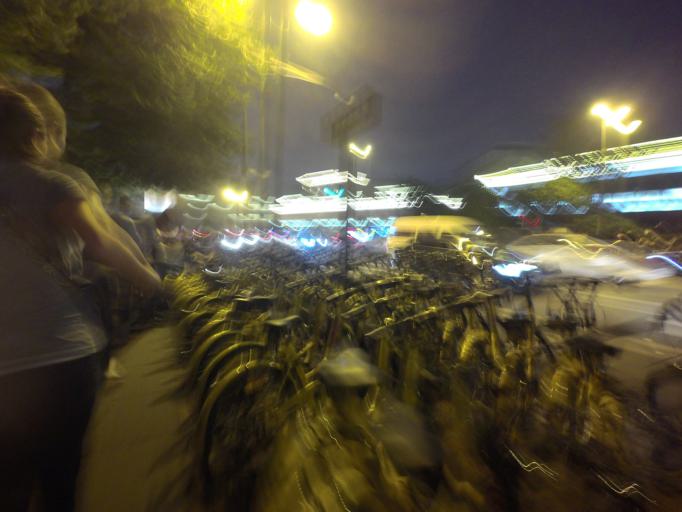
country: CN
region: Sichuan
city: Chengdu
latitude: 30.6468
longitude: 104.0465
